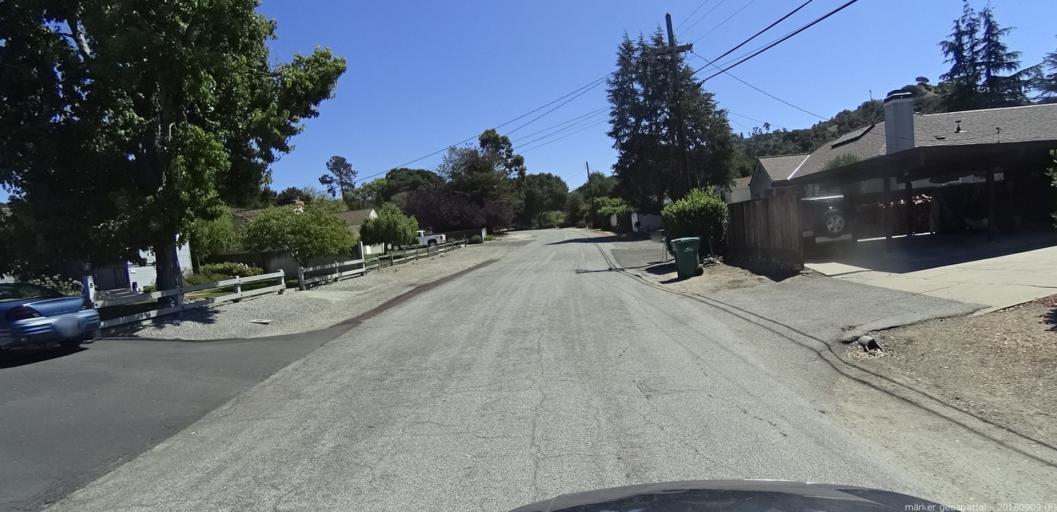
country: US
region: California
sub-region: Monterey County
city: Carmel Valley Village
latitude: 36.5763
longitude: -121.7207
